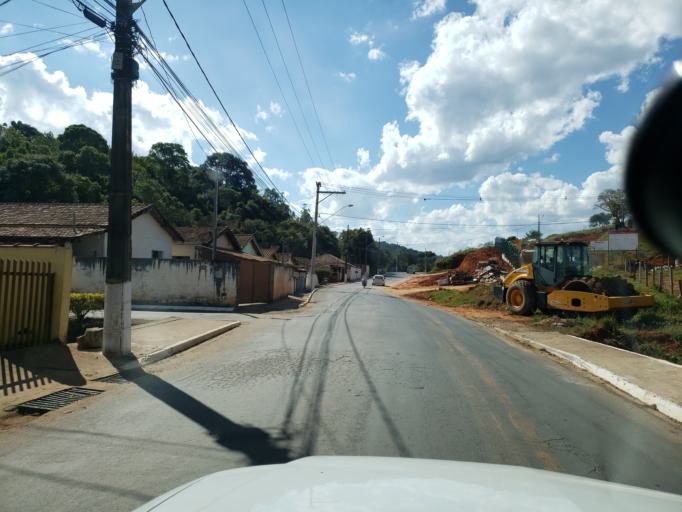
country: BR
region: Minas Gerais
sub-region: Monte Siao
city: Monte Siao
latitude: -22.4236
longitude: -46.5678
